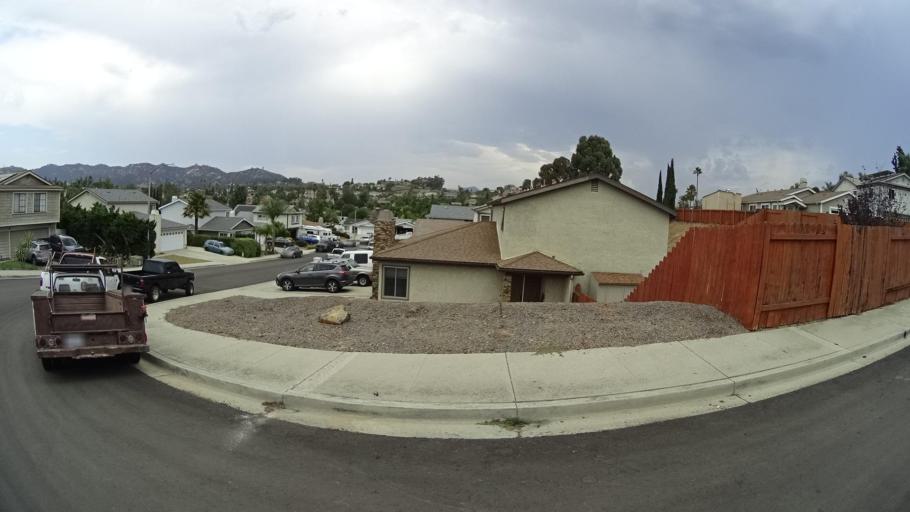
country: US
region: California
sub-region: San Diego County
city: Escondido
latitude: 33.1460
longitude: -117.1160
